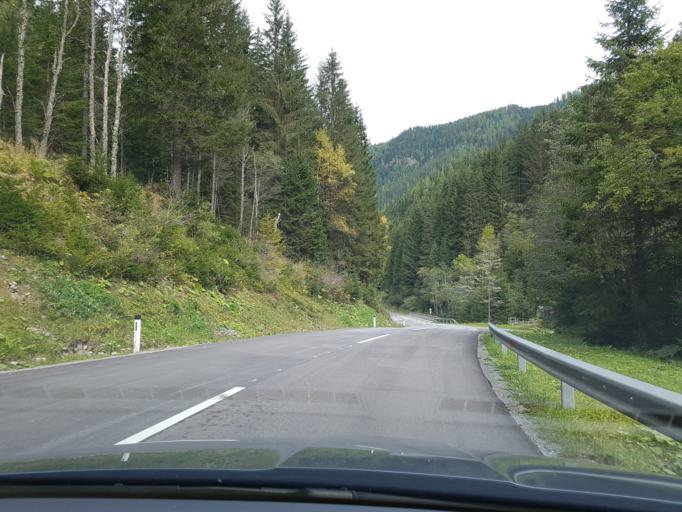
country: AT
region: Salzburg
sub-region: Politischer Bezirk Tamsweg
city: Ramingstein
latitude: 46.9874
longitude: 13.9058
